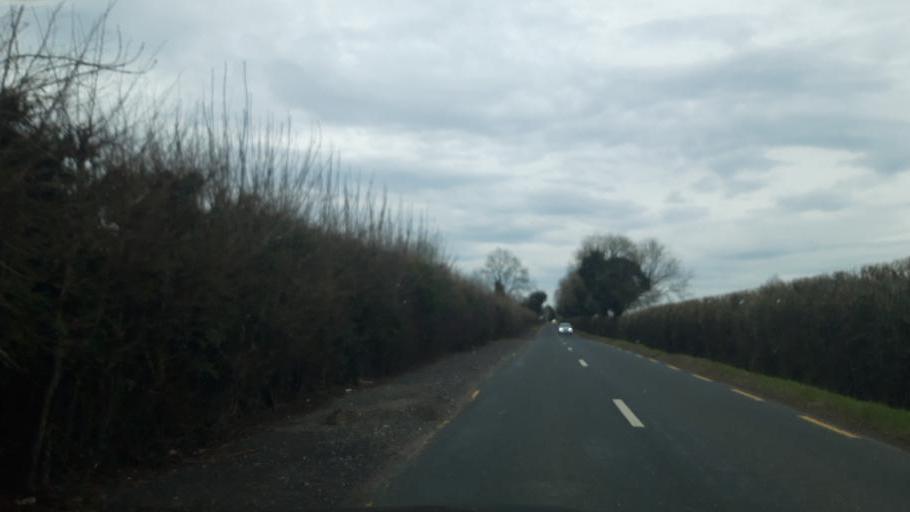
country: IE
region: Leinster
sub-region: Kildare
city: Clane
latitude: 53.3184
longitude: -6.7056
